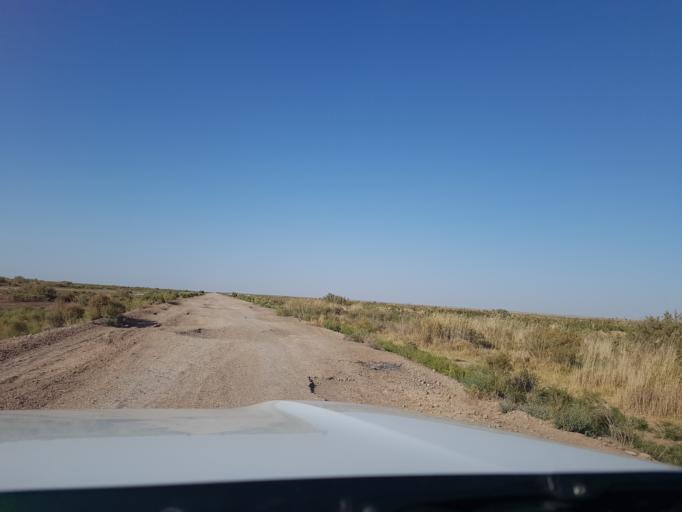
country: IR
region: Razavi Khorasan
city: Sarakhs
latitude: 36.9637
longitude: 61.3827
